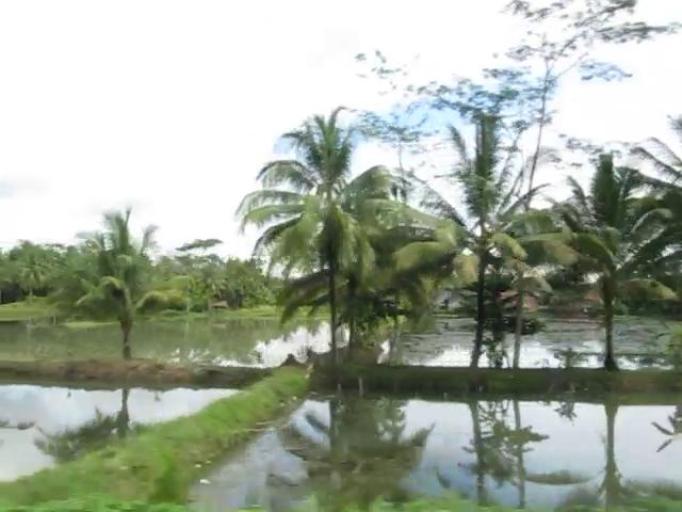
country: ID
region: Central Java
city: Meluwung
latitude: -7.3949
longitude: 108.6997
